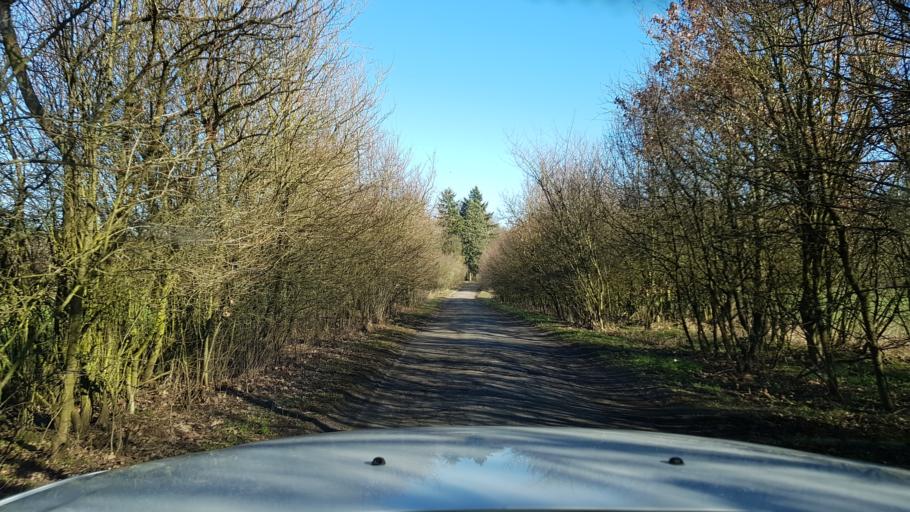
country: PL
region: West Pomeranian Voivodeship
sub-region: Powiat pyrzycki
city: Lipiany
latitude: 53.0241
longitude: 15.0116
